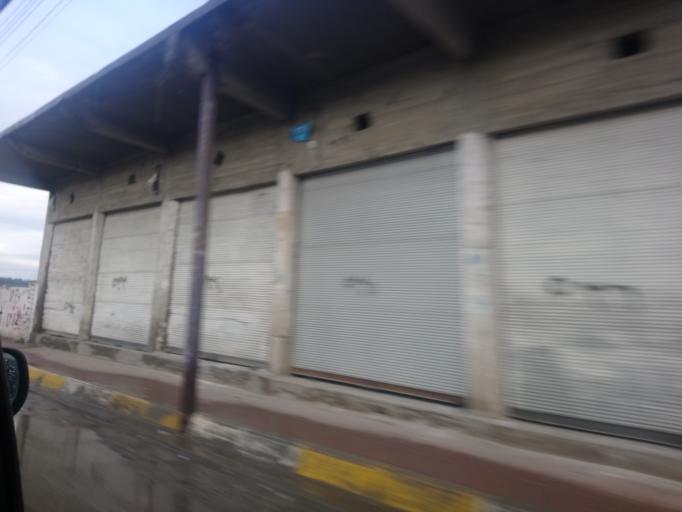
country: IQ
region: As Sulaymaniyah
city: Qeladize
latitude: 36.1847
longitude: 45.1194
